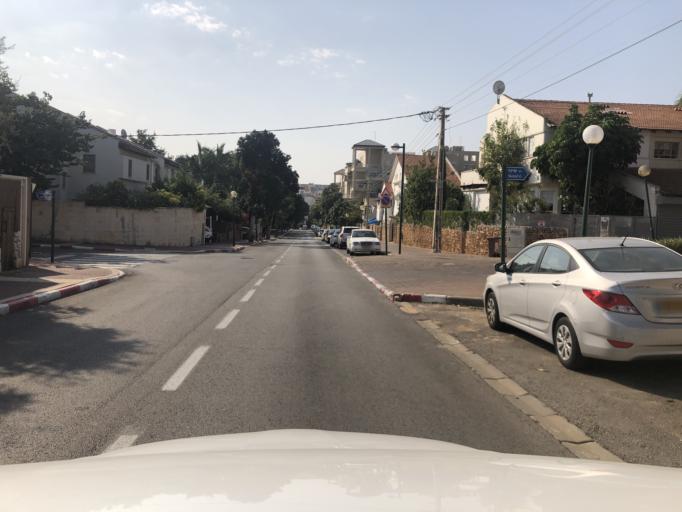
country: IL
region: Central District
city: Kfar Saba
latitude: 32.1820
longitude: 34.9071
